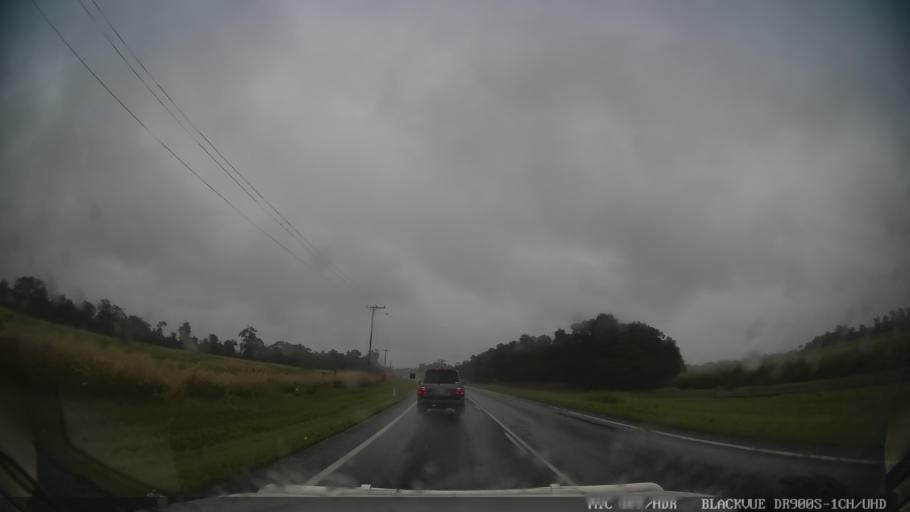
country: AU
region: Queensland
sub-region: Cassowary Coast
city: Innisfail
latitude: -17.6573
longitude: 146.0365
